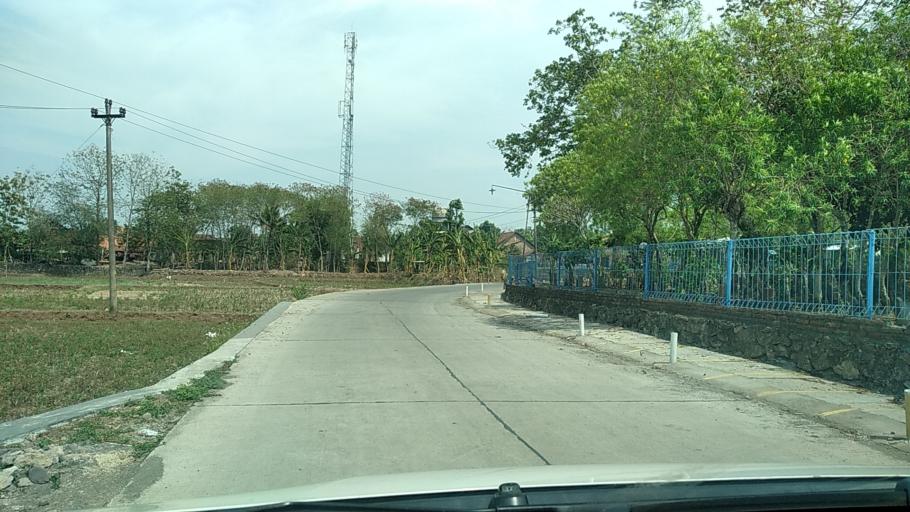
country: ID
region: Central Java
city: Mranggen
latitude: -7.0625
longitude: 110.4865
